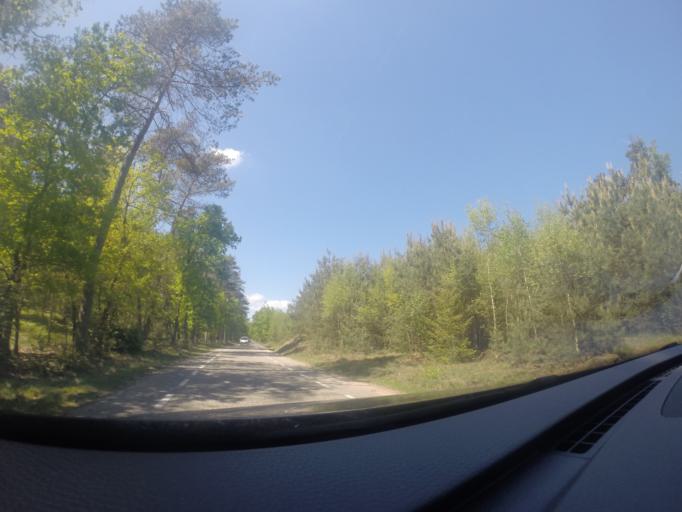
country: NL
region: Gelderland
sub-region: Gemeente Apeldoorn
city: Beekbergen
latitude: 52.1090
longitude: 5.9353
